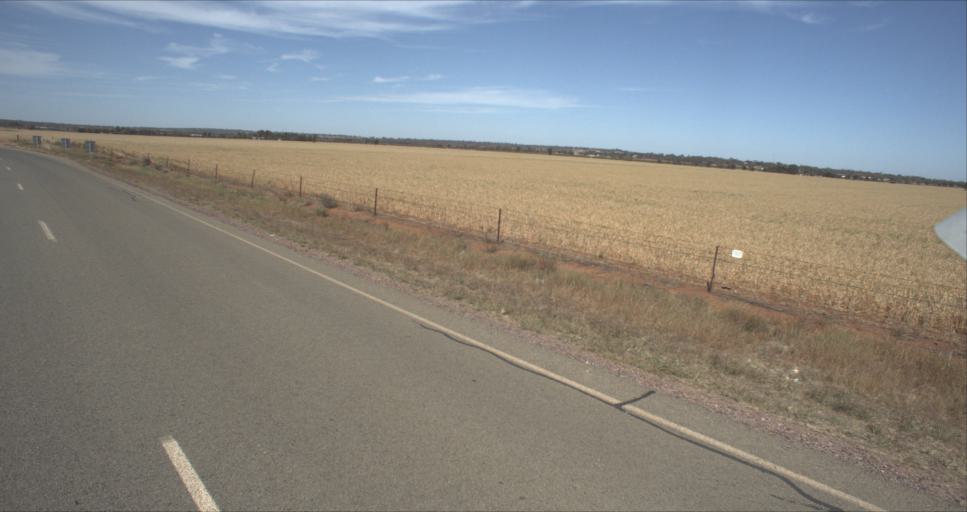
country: AU
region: New South Wales
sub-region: Leeton
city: Leeton
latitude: -34.5625
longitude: 146.4815
